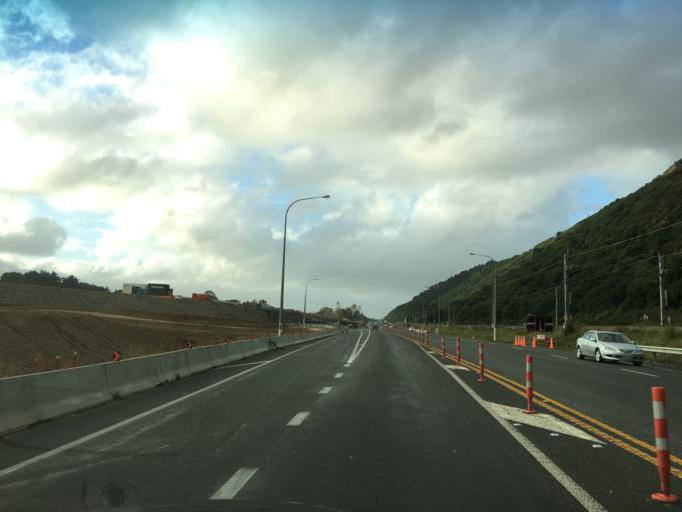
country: NZ
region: Wellington
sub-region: Kapiti Coast District
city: Paraparaumu
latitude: -40.9411
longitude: 174.9929
